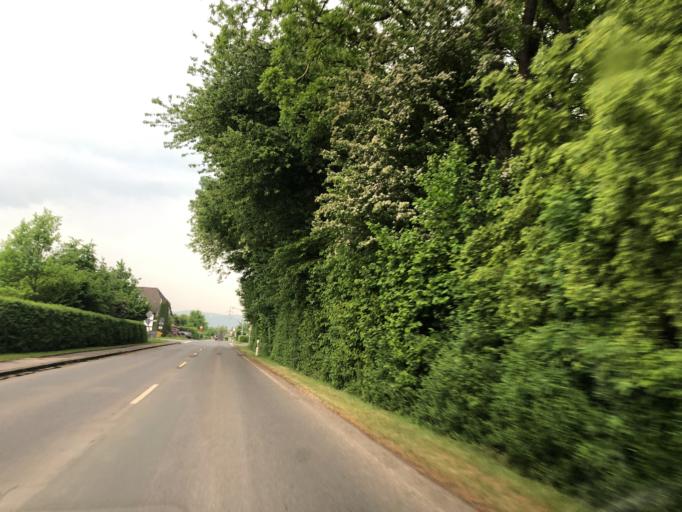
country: DE
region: North Rhine-Westphalia
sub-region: Regierungsbezirk Detmold
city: Dorentrup
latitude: 52.0158
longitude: 9.0177
